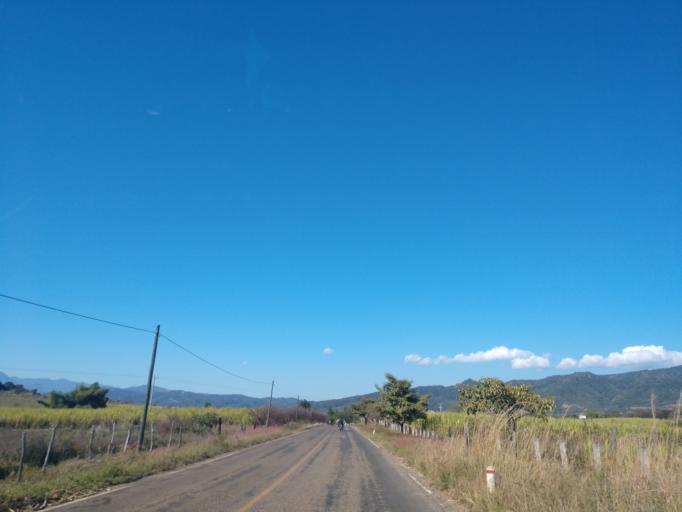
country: MX
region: Nayarit
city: Compostela
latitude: 21.2661
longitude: -104.8925
